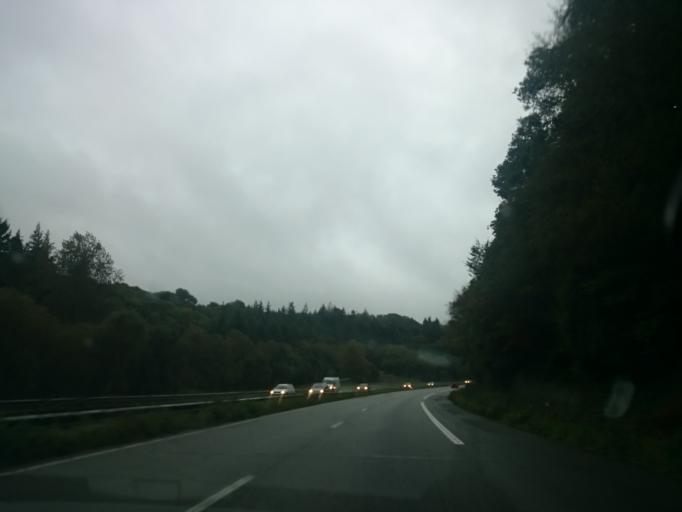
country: FR
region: Brittany
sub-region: Departement du Finistere
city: Chateaulin
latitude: 48.1787
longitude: -4.0441
